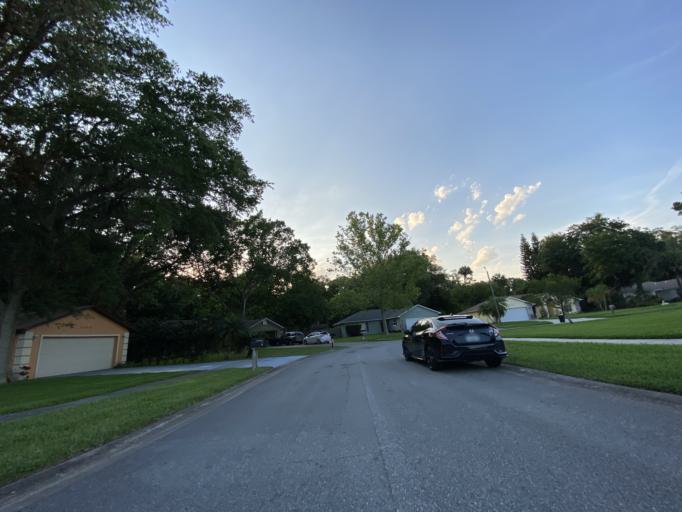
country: US
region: Florida
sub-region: Volusia County
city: Port Orange
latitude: 29.1427
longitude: -81.0061
